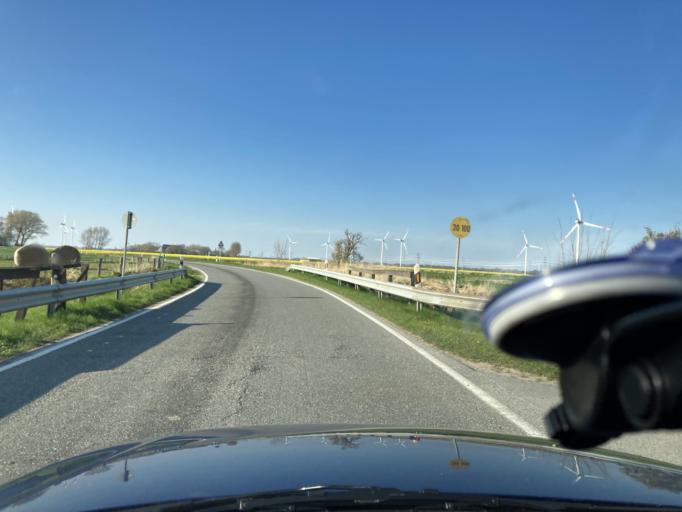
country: DE
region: Schleswig-Holstein
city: Lieth
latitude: 54.1604
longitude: 9.0338
